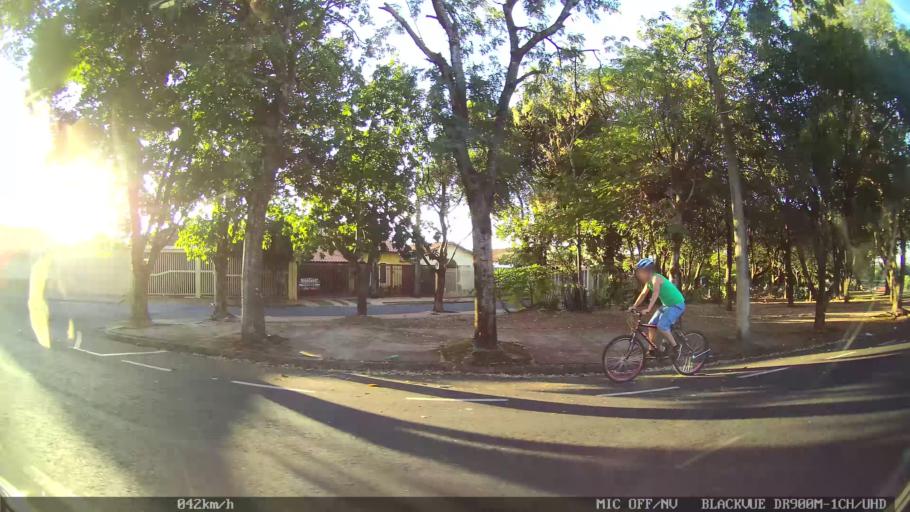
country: BR
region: Sao Paulo
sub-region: Sao Jose Do Rio Preto
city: Sao Jose do Rio Preto
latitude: -20.7800
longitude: -49.3642
